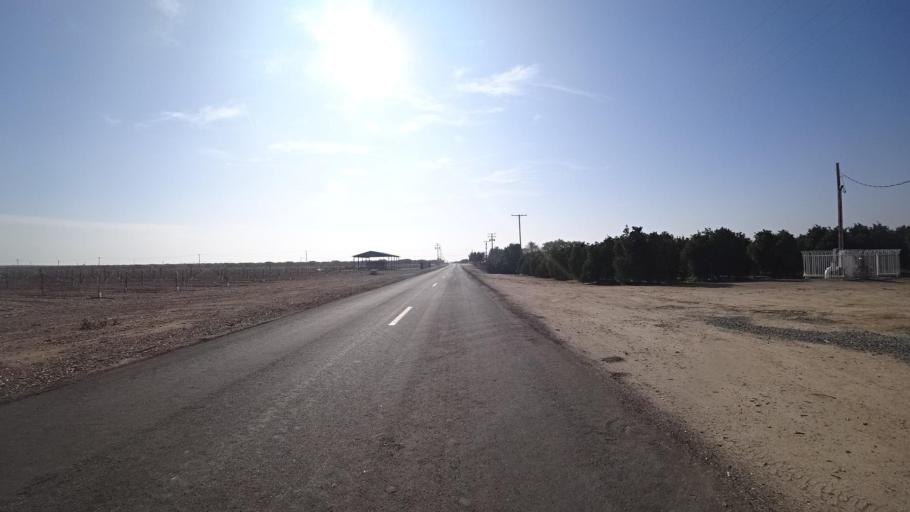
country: US
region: California
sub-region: Kern County
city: McFarland
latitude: 35.6770
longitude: -119.1693
